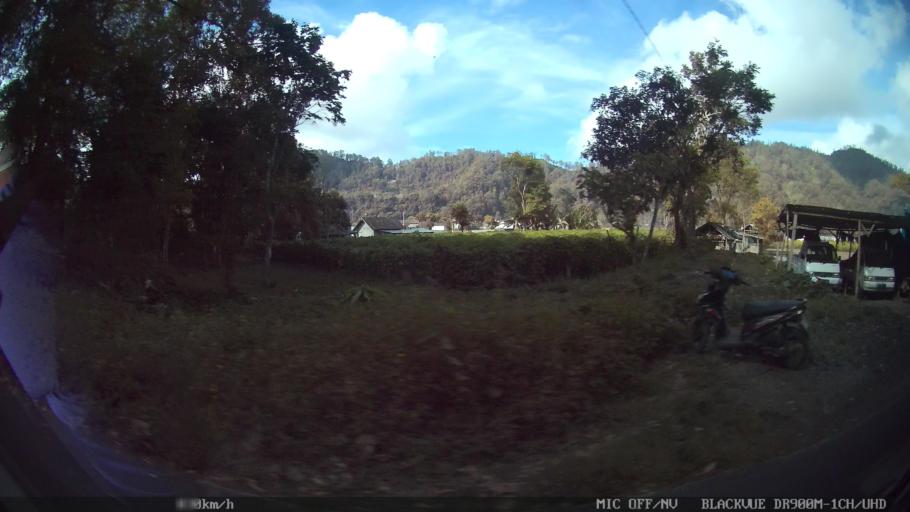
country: ID
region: Bali
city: Banjar Trunyan
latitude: -8.2252
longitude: 115.4113
